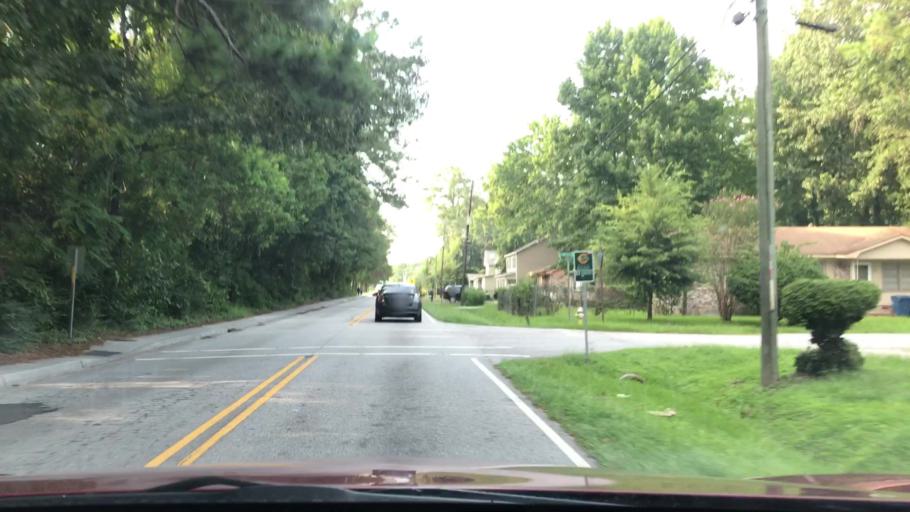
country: US
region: South Carolina
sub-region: Charleston County
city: North Charleston
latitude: 32.8028
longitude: -80.0293
